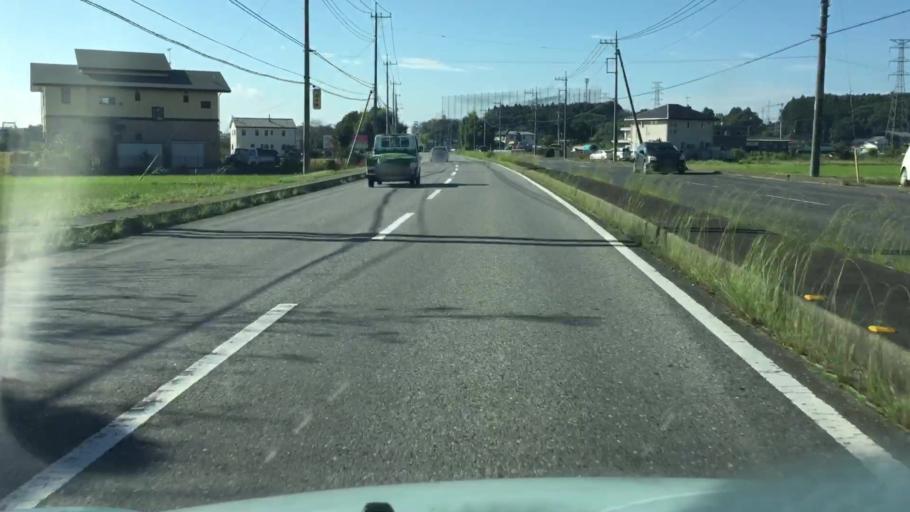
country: JP
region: Tochigi
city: Ujiie
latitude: 36.6329
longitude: 139.9944
